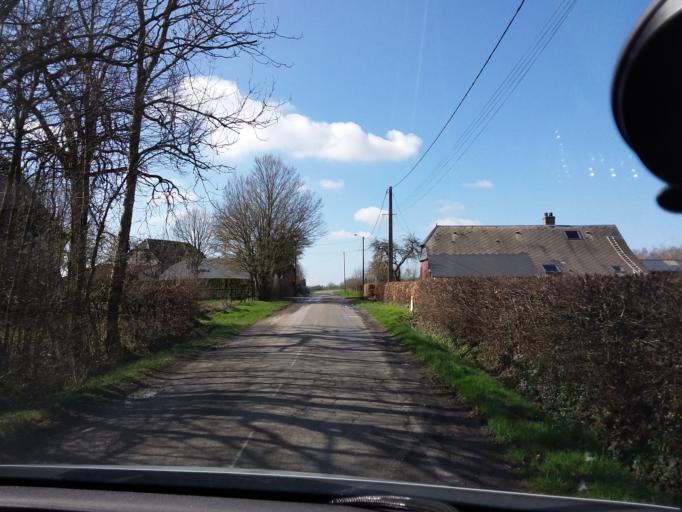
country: FR
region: Picardie
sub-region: Departement de l'Aisne
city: Origny-en-Thierache
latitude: 49.8373
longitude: 4.0607
